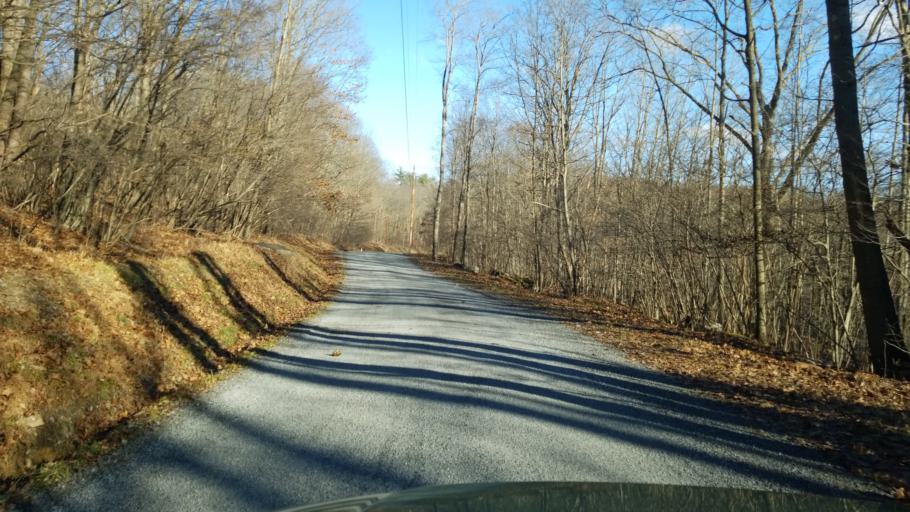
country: US
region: Pennsylvania
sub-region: Jefferson County
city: Brockway
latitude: 41.2789
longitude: -78.8219
